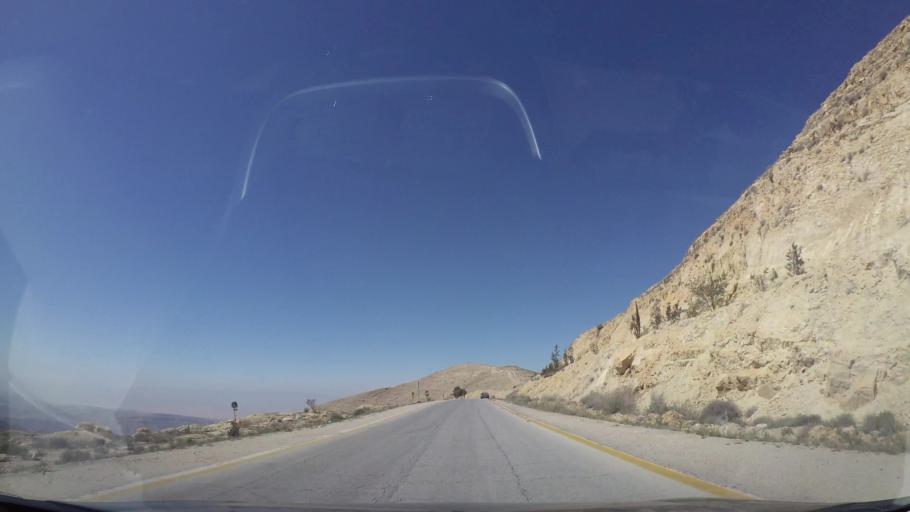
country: JO
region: Tafielah
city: At Tafilah
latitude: 30.8563
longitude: 35.5470
